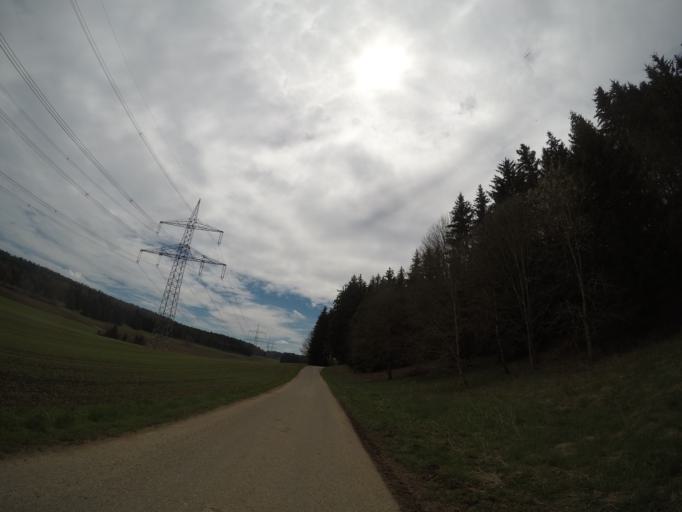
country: DE
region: Baden-Wuerttemberg
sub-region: Tuebingen Region
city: Laichingen
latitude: 48.4948
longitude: 9.6558
